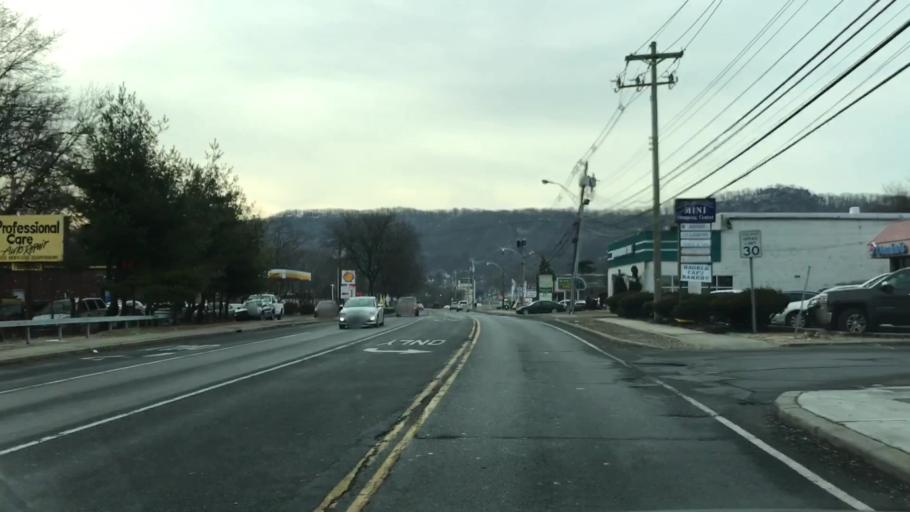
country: US
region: New York
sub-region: Rockland County
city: West Haverstraw
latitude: 41.2094
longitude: -73.9855
